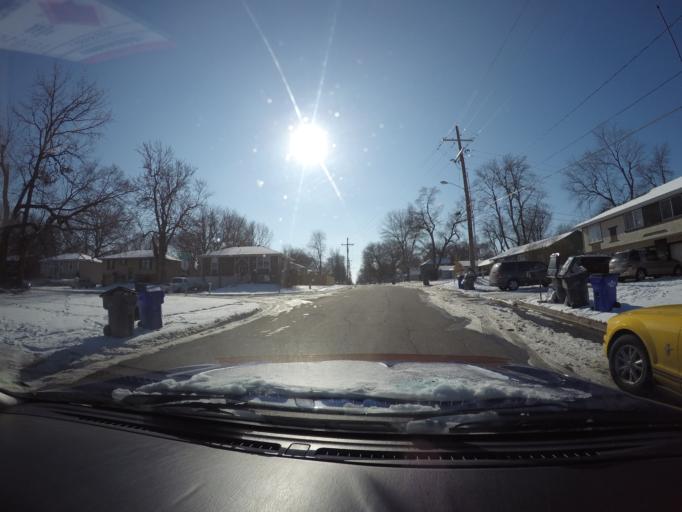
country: US
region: Kansas
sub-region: Johnson County
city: Olathe
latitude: 38.8911
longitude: -94.8253
